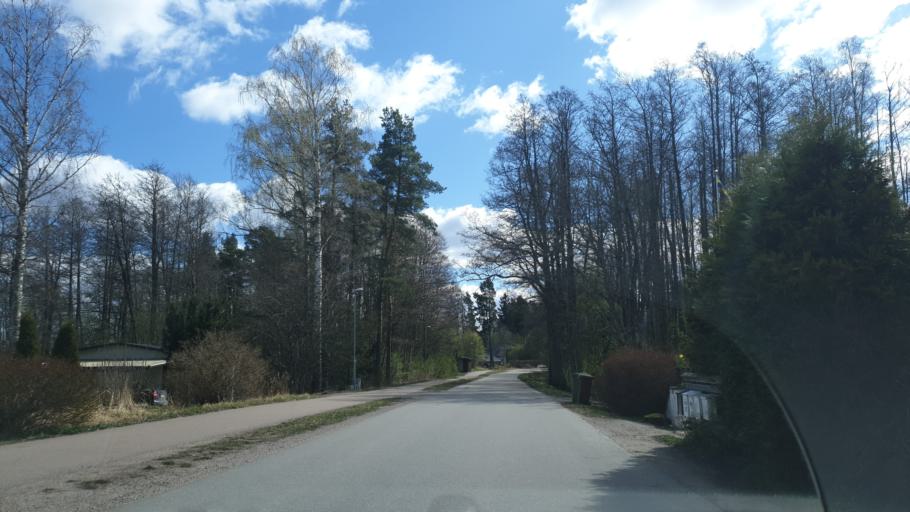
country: SE
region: Vaestmanland
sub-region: Kopings Kommun
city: Koping
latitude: 59.4845
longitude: 16.0543
